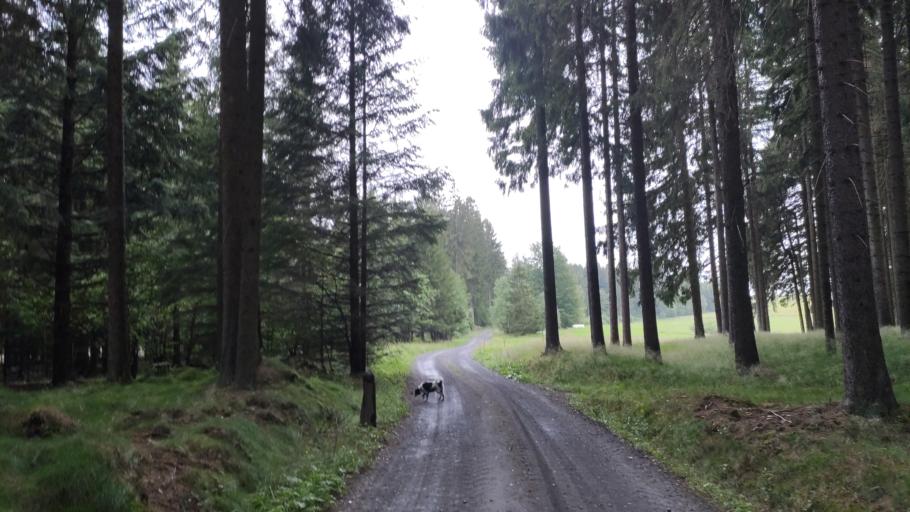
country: DE
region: Bavaria
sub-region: Upper Franconia
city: Reichenbach
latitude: 50.4557
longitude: 11.4164
